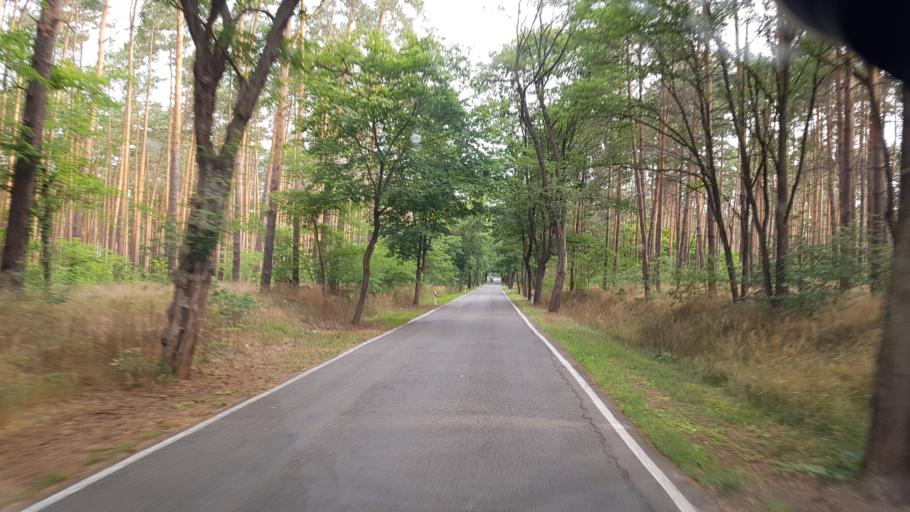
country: DE
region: Brandenburg
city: Dahme
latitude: 51.9301
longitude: 13.3971
